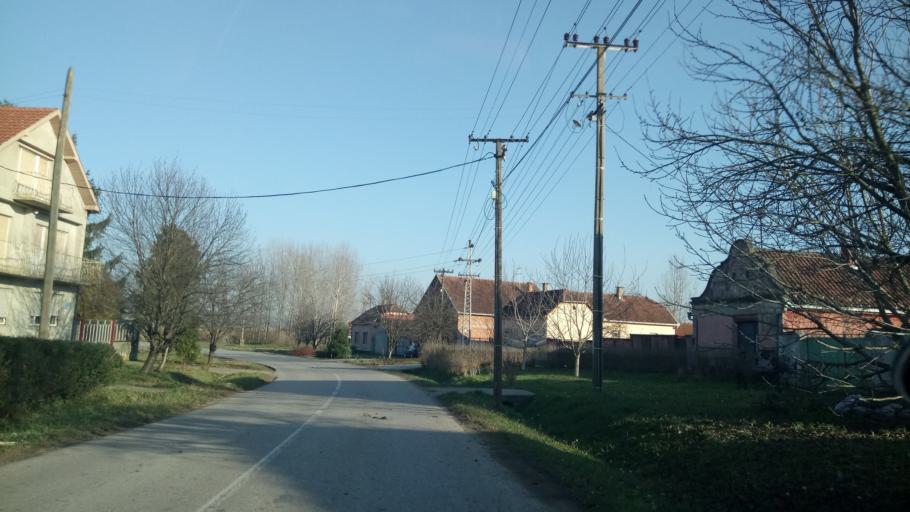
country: RS
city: Krcedin
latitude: 45.1402
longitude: 20.1389
